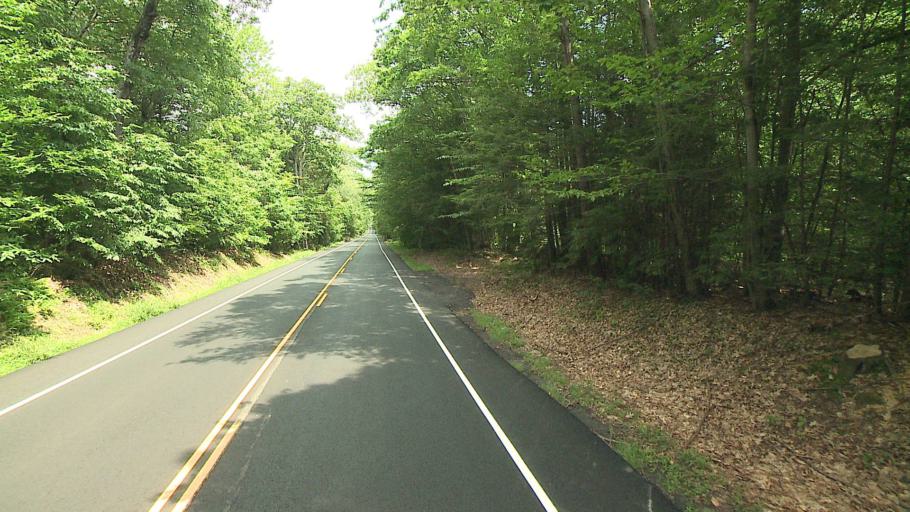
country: US
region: Connecticut
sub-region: Hartford County
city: North Granby
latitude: 42.0041
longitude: -72.8958
